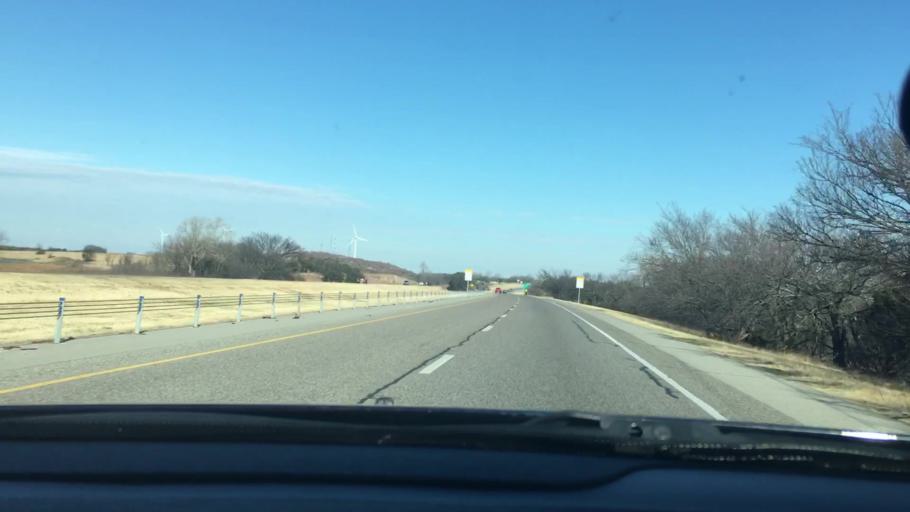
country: US
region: Oklahoma
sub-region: Murray County
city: Davis
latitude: 34.3879
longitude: -97.1415
